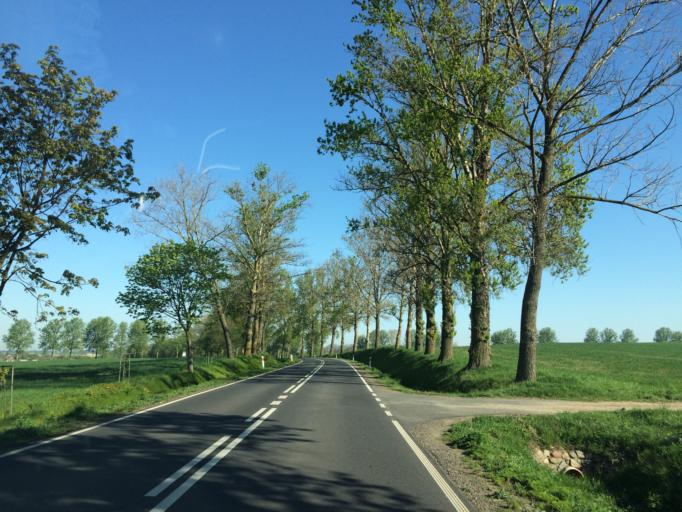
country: PL
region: Warmian-Masurian Voivodeship
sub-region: Powiat ilawski
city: Lubawa
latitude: 53.4162
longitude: 19.7902
